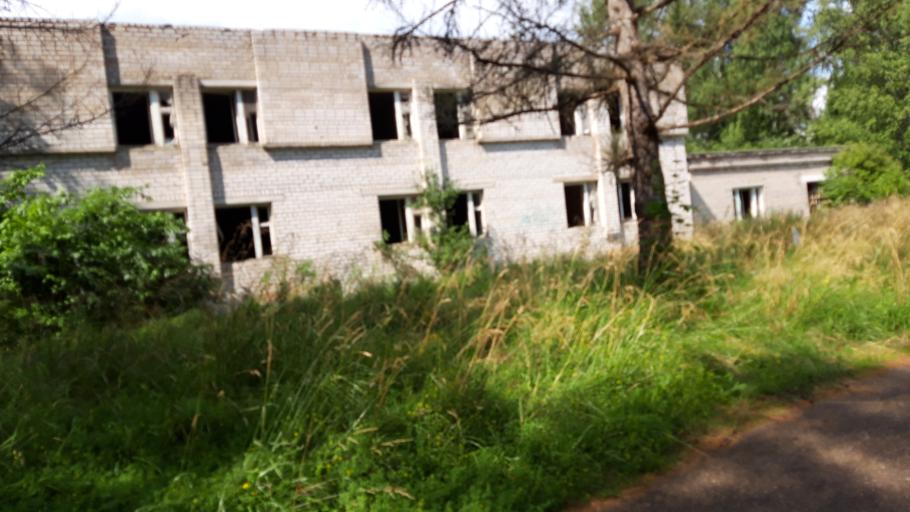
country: RU
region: Tverskaya
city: Konakovo
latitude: 56.6674
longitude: 36.6844
